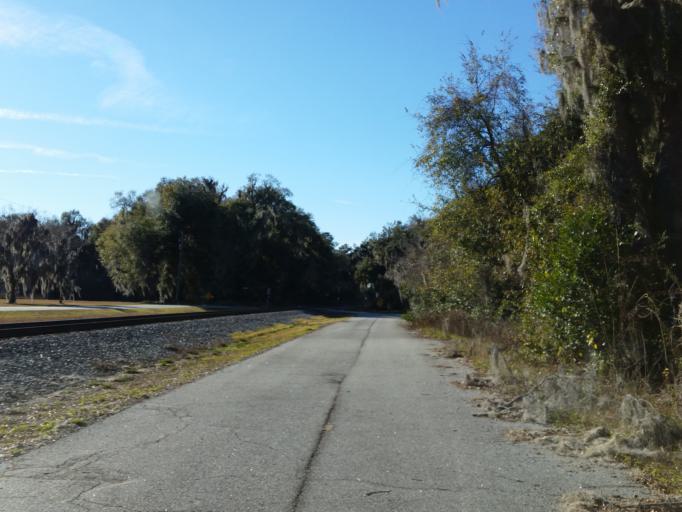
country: US
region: Georgia
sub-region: Echols County
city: Statenville
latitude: 30.6842
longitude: -83.1875
